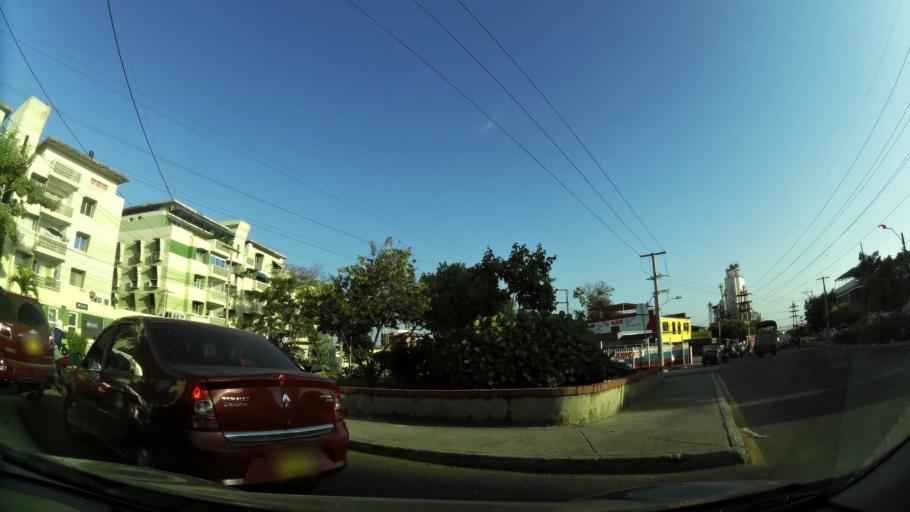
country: CO
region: Bolivar
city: Cartagena
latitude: 10.3899
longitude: -75.5159
